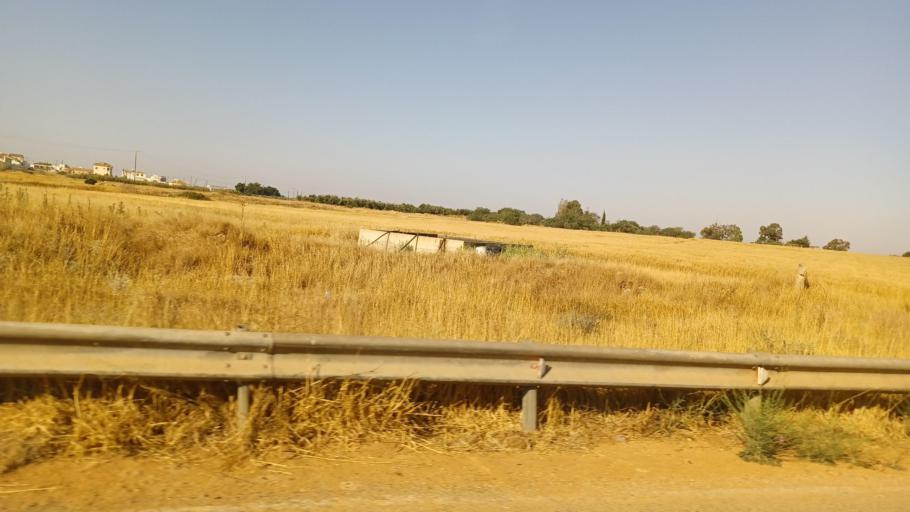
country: CY
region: Ammochostos
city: Frenaros
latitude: 35.0516
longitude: 33.9163
